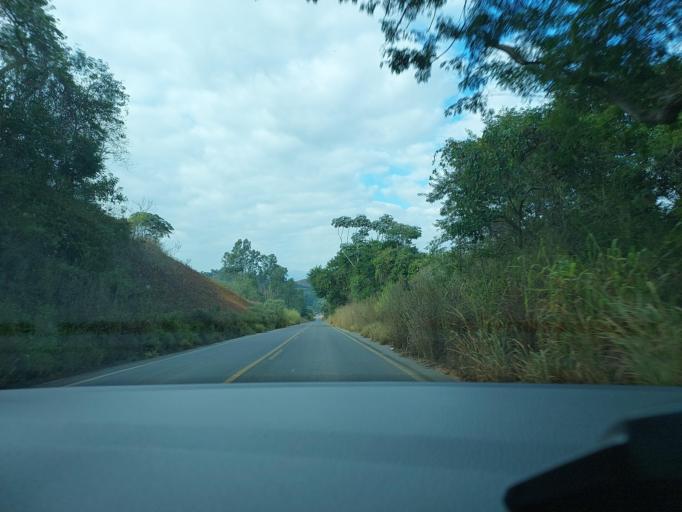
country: BR
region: Minas Gerais
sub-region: Vicosa
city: Vicosa
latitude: -20.8389
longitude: -42.7009
